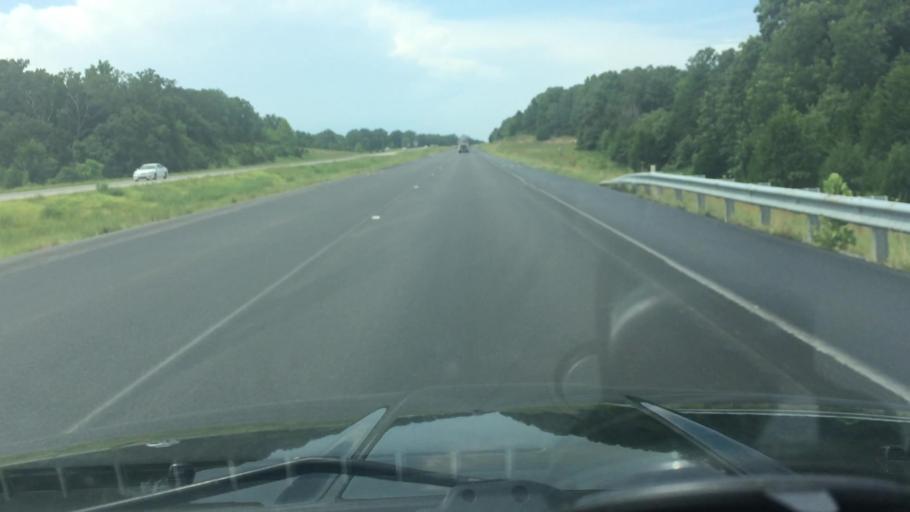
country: US
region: Missouri
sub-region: Saint Clair County
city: Osceola
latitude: 37.9468
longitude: -93.6370
